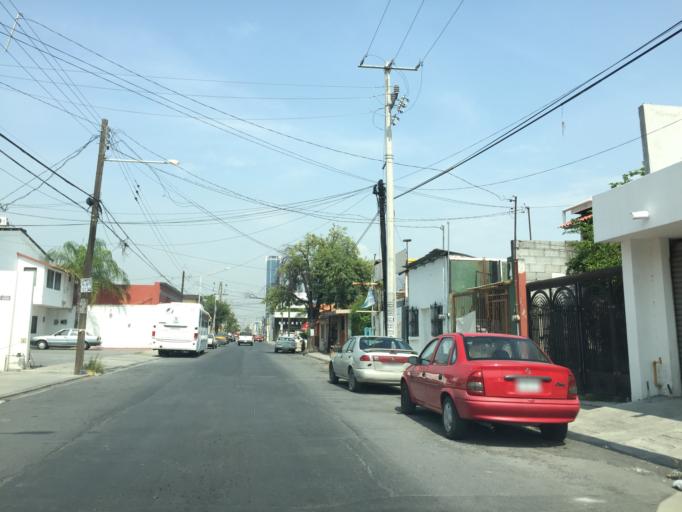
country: MX
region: Nuevo Leon
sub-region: Monterrey
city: Monterrey
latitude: 25.6618
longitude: -100.3022
